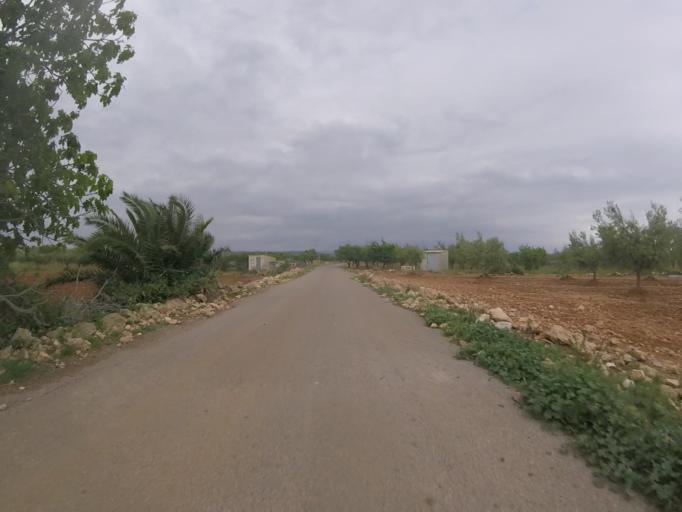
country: ES
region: Valencia
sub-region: Provincia de Castello
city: Torreblanca
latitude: 40.2147
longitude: 0.2371
